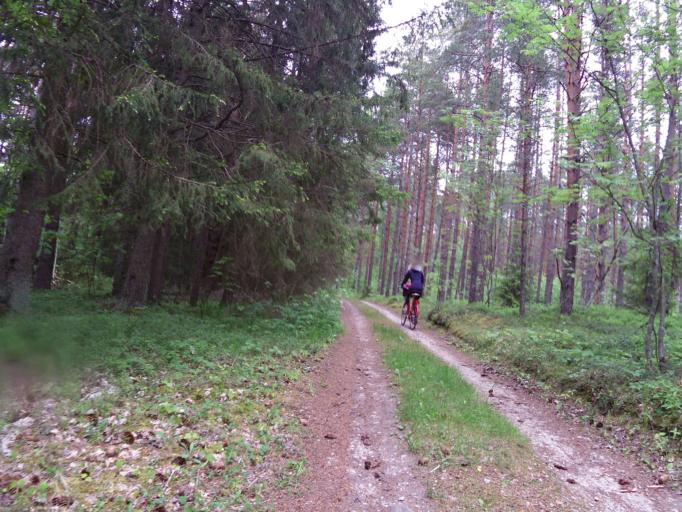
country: EE
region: Harju
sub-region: Paldiski linn
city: Paldiski
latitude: 59.2517
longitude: 23.7496
